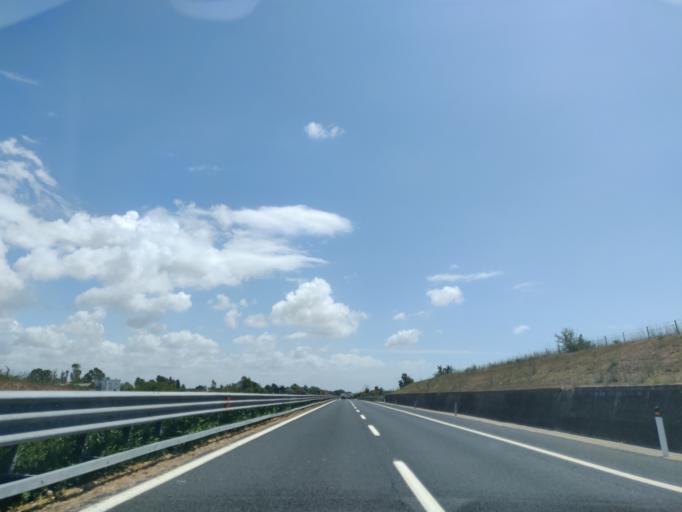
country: IT
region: Latium
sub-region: Citta metropolitana di Roma Capitale
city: Npp 23 (Parco Leonardo)
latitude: 41.8383
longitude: 12.2807
